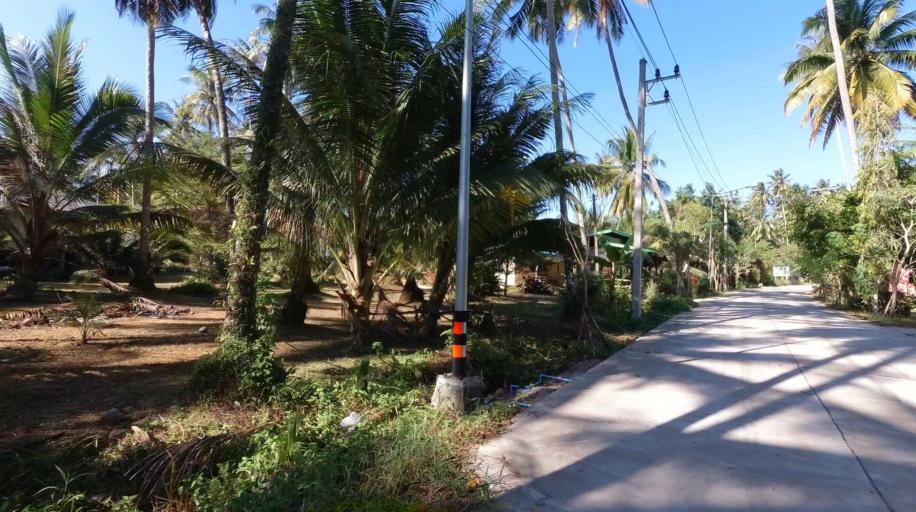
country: TH
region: Trat
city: Ko Kut
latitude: 11.6217
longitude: 102.5480
